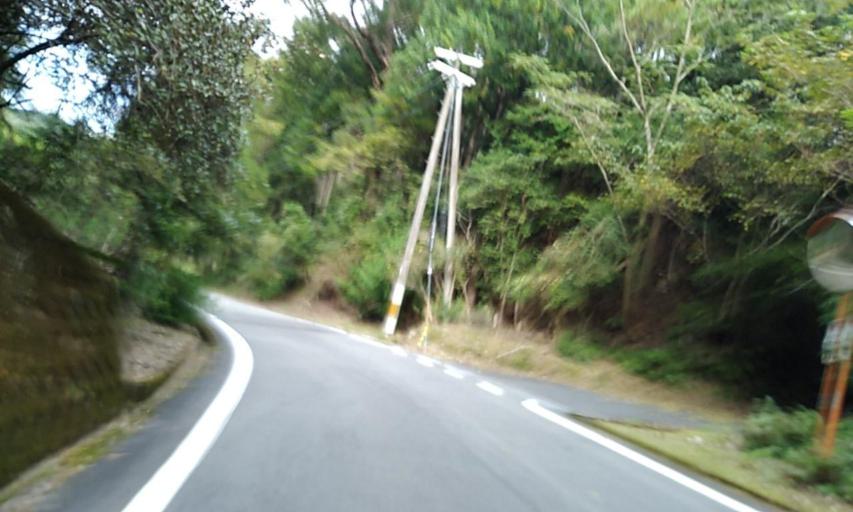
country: JP
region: Wakayama
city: Shingu
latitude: 33.5402
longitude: 135.8376
